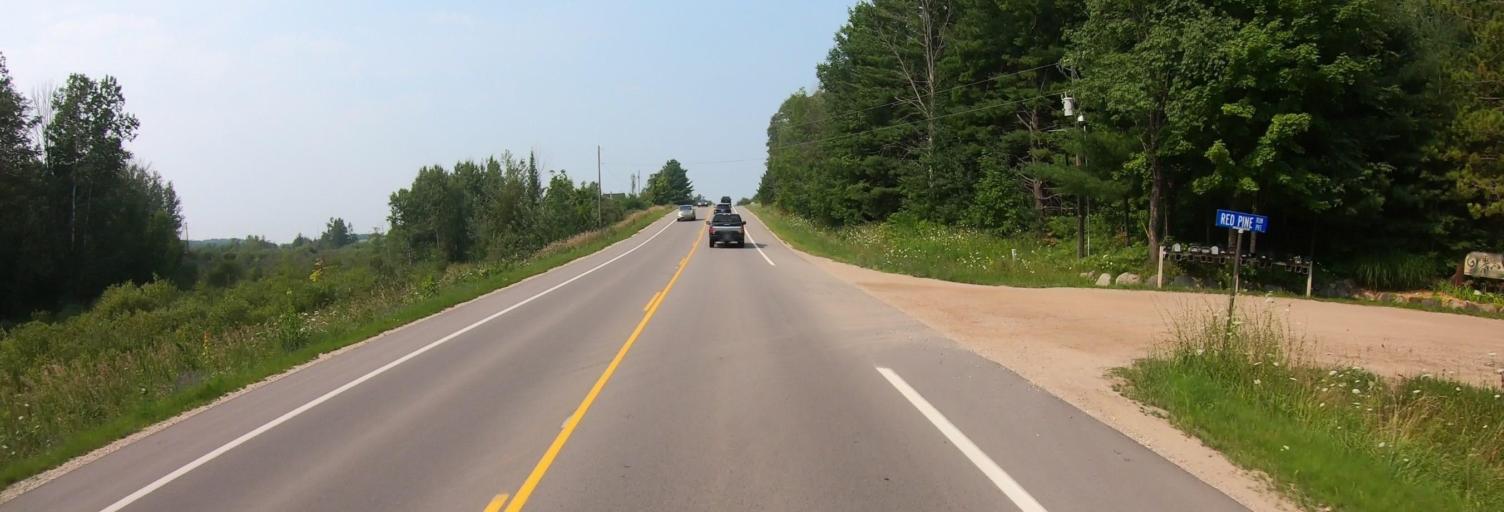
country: US
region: Michigan
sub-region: Charlevoix County
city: Charlevoix
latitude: 45.2281
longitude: -85.2613
